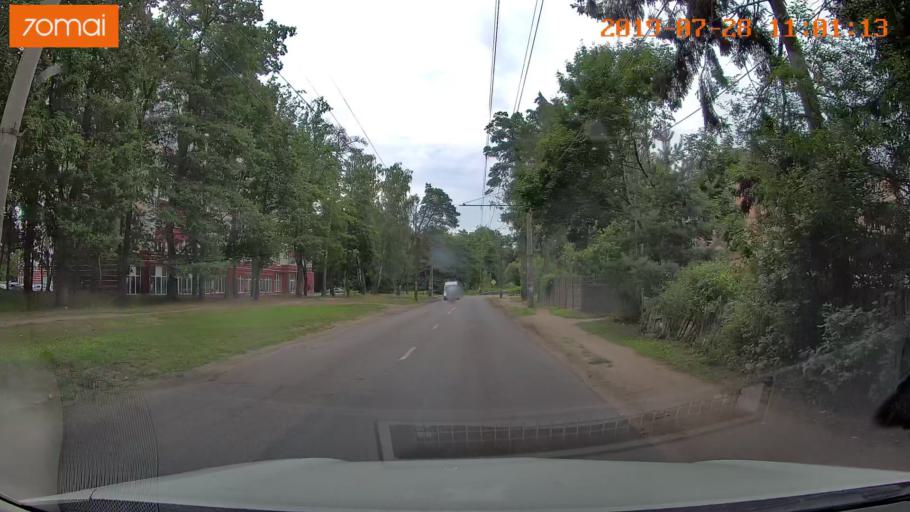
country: RU
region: Kaliningrad
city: Vzmorye
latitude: 54.7228
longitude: 20.3672
